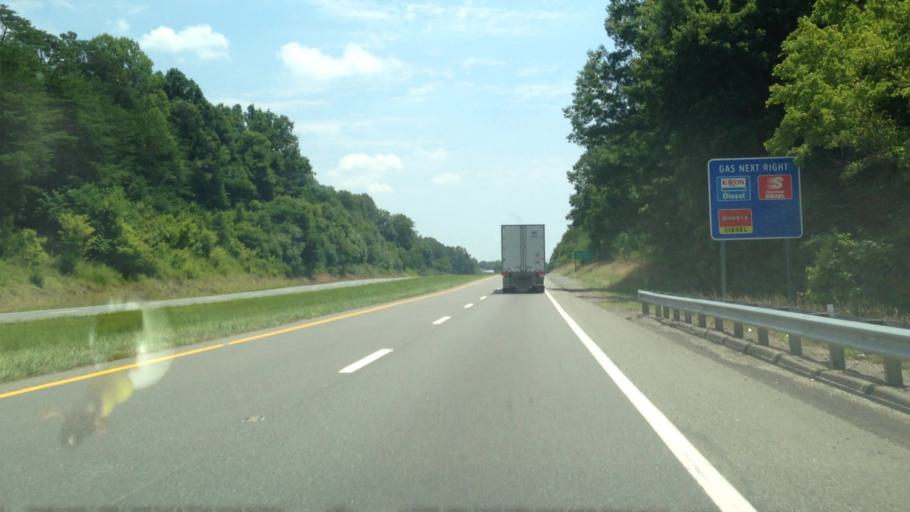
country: US
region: Virginia
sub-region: Henry County
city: Chatmoss
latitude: 36.6247
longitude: -79.8701
